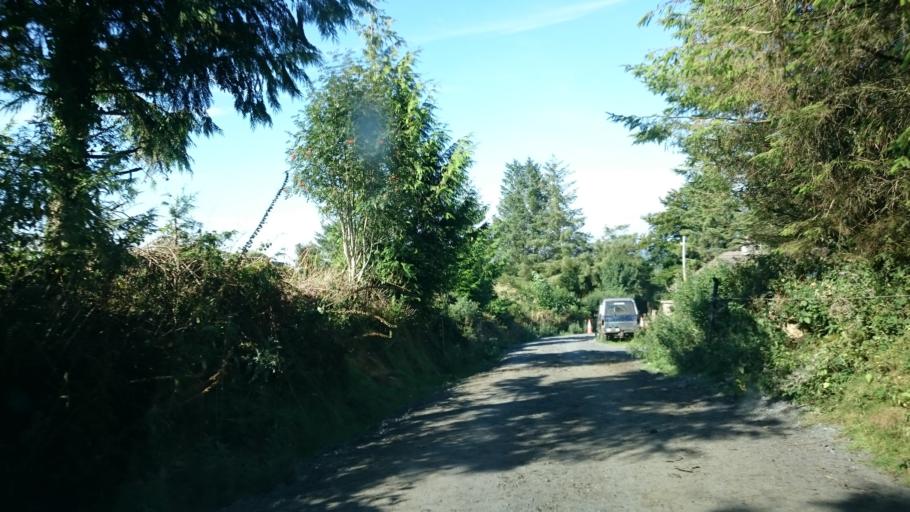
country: IE
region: Leinster
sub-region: Kilkenny
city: Graiguenamanagh
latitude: 52.5236
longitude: -6.9633
